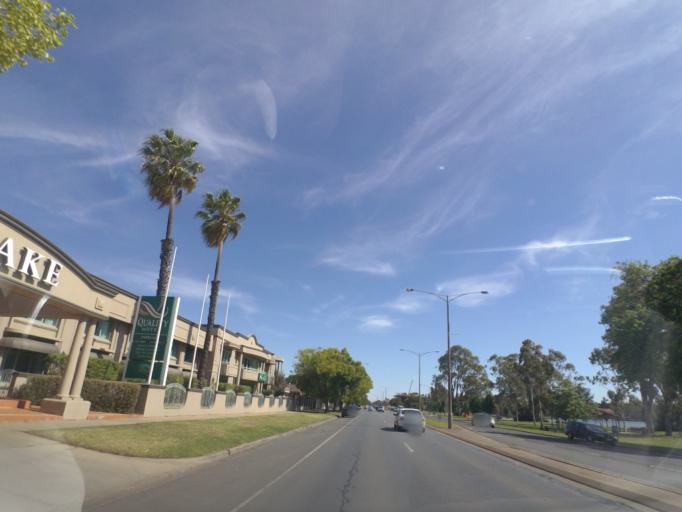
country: AU
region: Victoria
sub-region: Greater Shepparton
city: Shepparton
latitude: -36.3867
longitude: 145.3982
